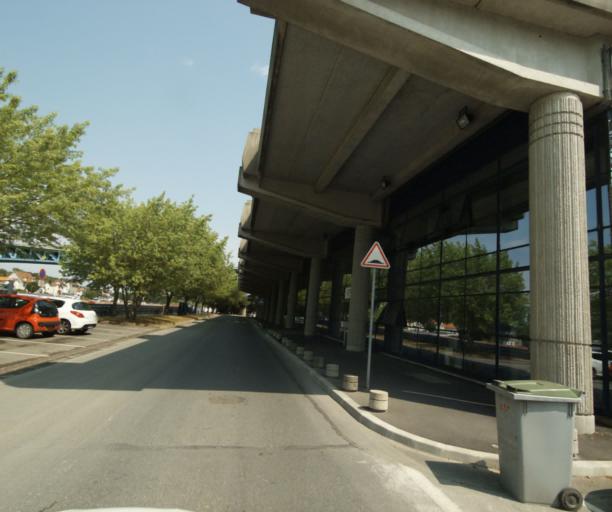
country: FR
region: Ile-de-France
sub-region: Departement des Yvelines
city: Maurecourt
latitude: 48.9908
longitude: 2.0732
